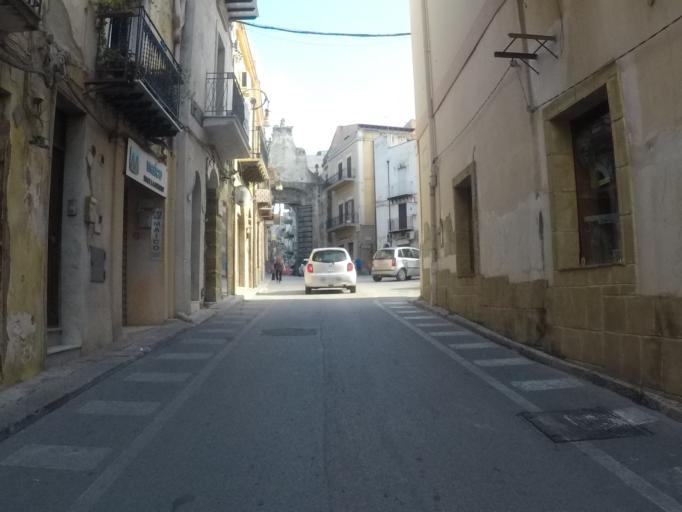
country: IT
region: Sicily
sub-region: Agrigento
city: Sciacca
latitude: 37.5102
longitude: 13.0791
